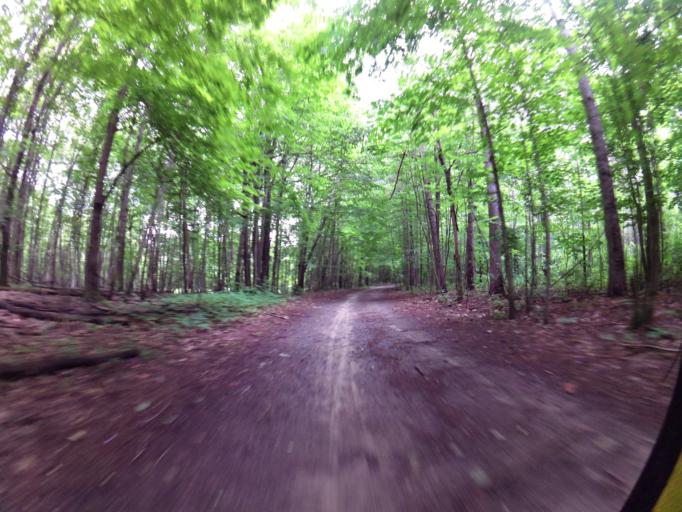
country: CA
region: Ontario
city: Bells Corners
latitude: 45.3030
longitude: -75.8489
